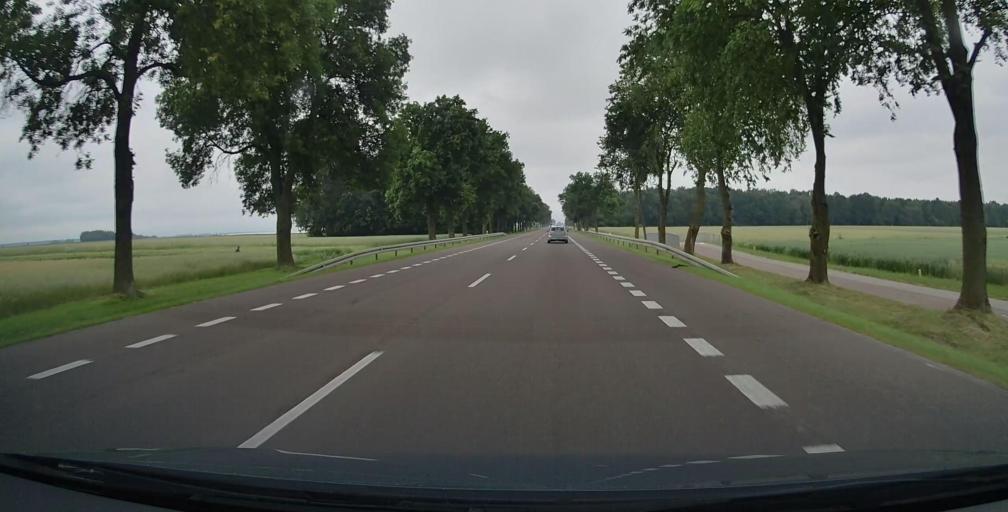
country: PL
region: Lublin Voivodeship
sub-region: Powiat bialski
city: Rzeczyca
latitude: 52.0143
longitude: 22.7340
